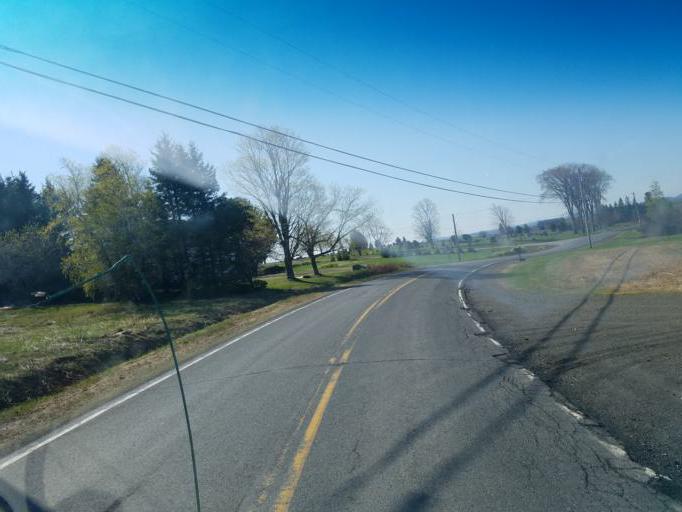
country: US
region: Maine
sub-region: Aroostook County
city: Caribou
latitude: 46.8684
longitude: -68.2091
